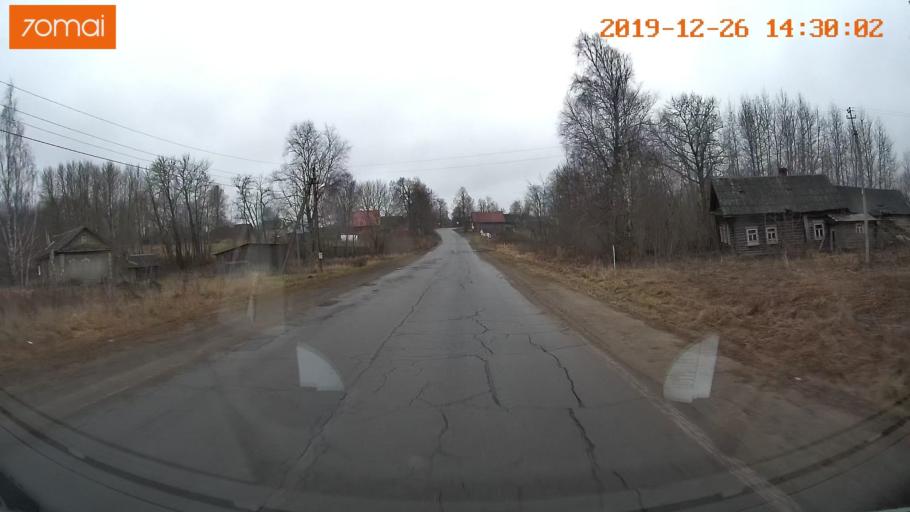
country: RU
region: Jaroslavl
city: Poshekhon'ye
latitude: 58.4573
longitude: 39.0390
